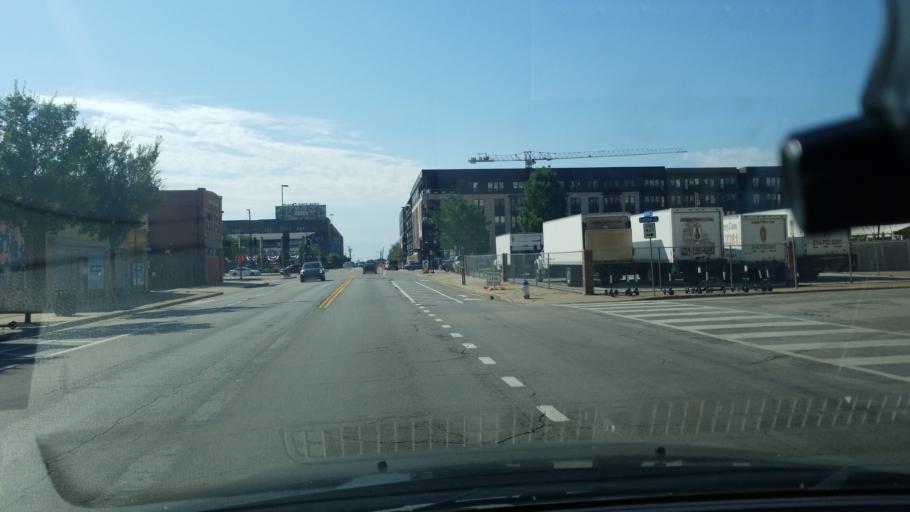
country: US
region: Texas
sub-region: Dallas County
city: Dallas
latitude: 32.7786
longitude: -96.7922
